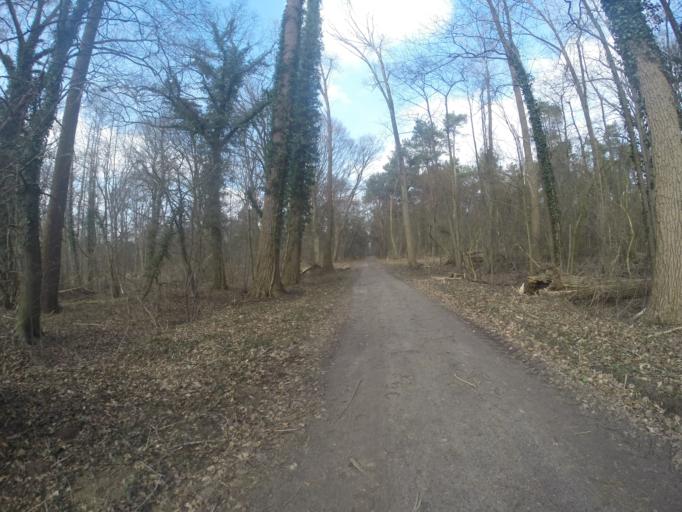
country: NL
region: Gelderland
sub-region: Gemeente Lochem
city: Almen
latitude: 52.1281
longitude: 6.3217
